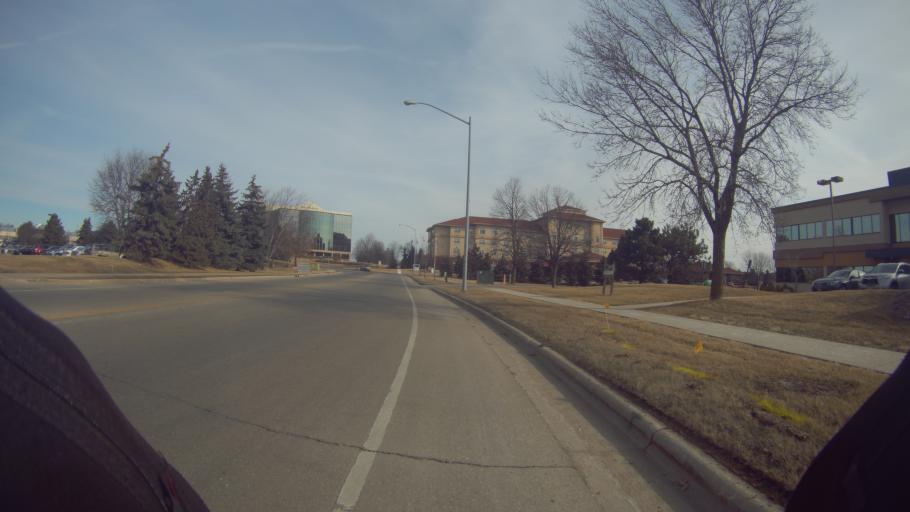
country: US
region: Wisconsin
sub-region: Dane County
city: Middleton
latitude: 43.0808
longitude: -89.5243
